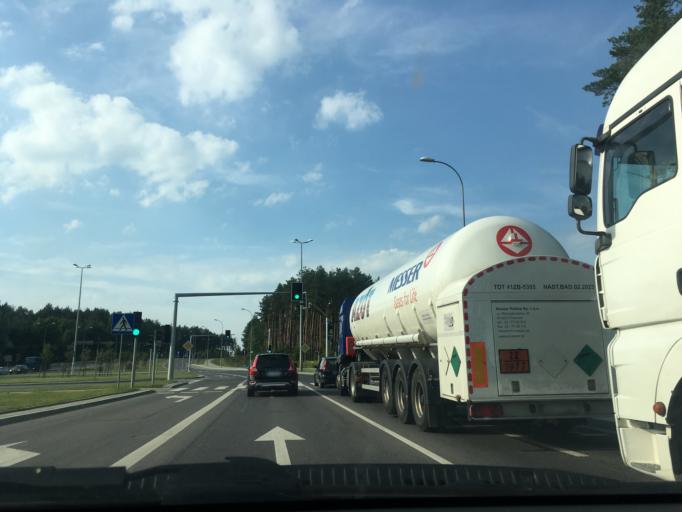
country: PL
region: Podlasie
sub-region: Bialystok
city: Bialystok
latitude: 53.1285
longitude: 23.2239
